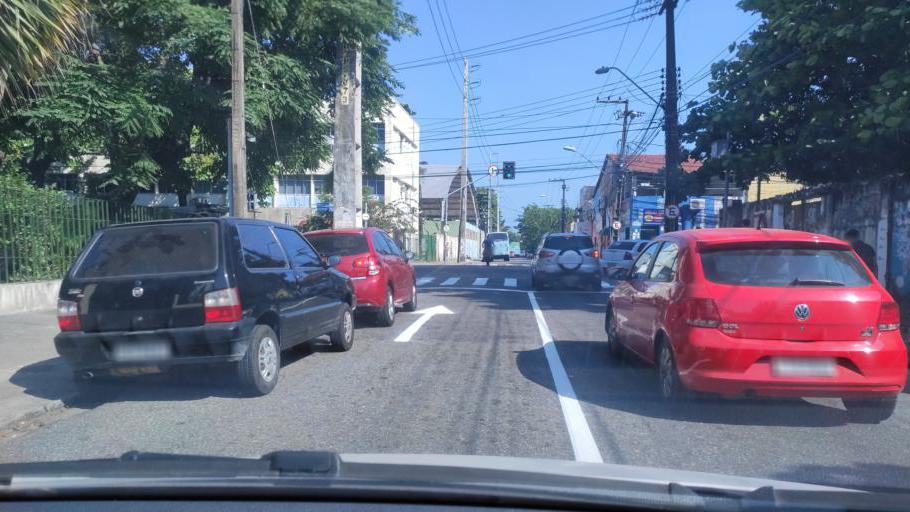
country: BR
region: Ceara
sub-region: Fortaleza
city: Fortaleza
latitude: -3.7401
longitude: -38.5379
